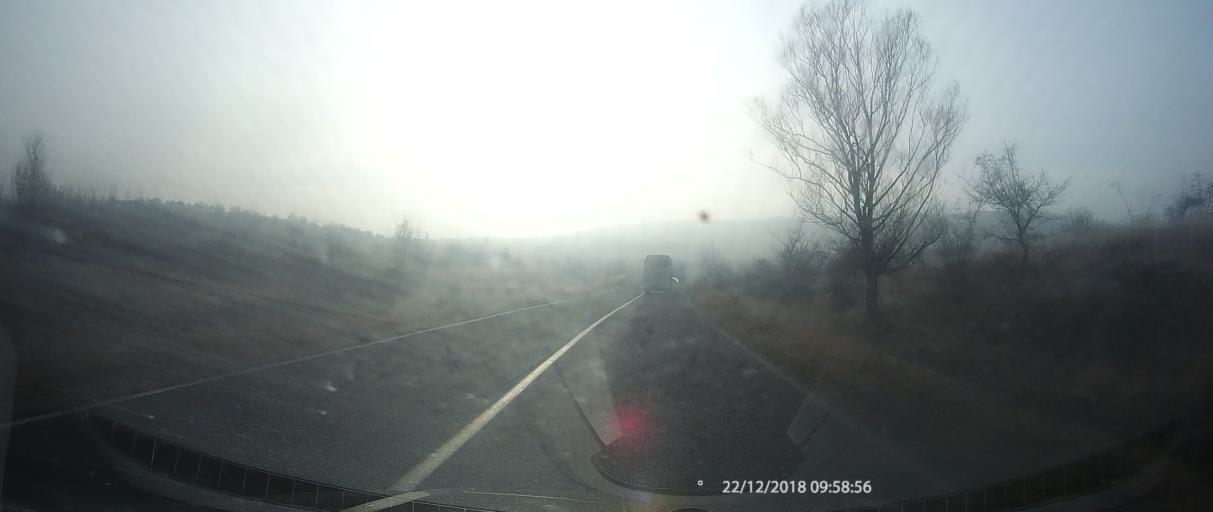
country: MK
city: Klechovce
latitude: 42.1549
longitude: 21.9510
